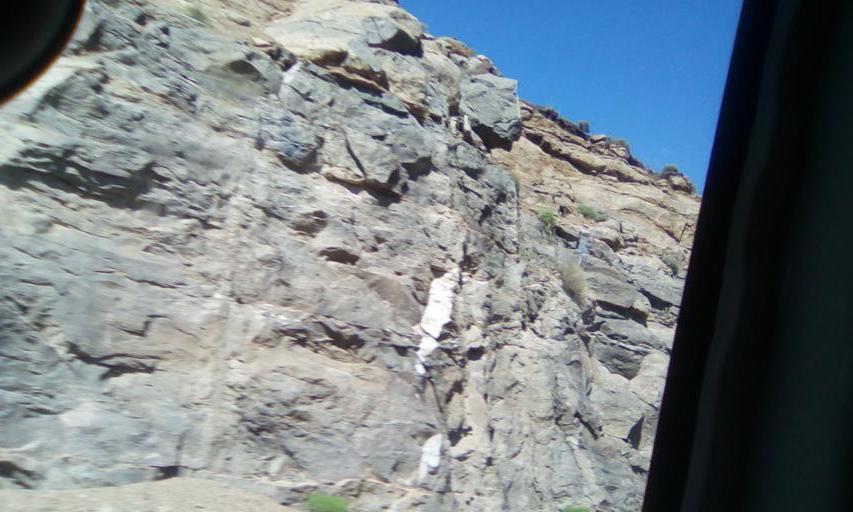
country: LS
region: Maseru
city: Nako
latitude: -29.8898
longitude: 28.1158
